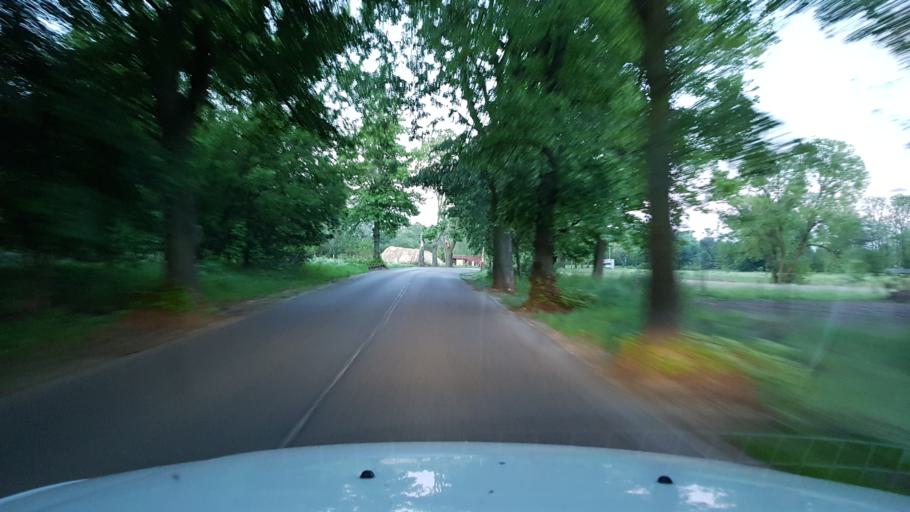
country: PL
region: West Pomeranian Voivodeship
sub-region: Powiat goleniowski
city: Goleniow
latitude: 53.5523
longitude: 14.8547
